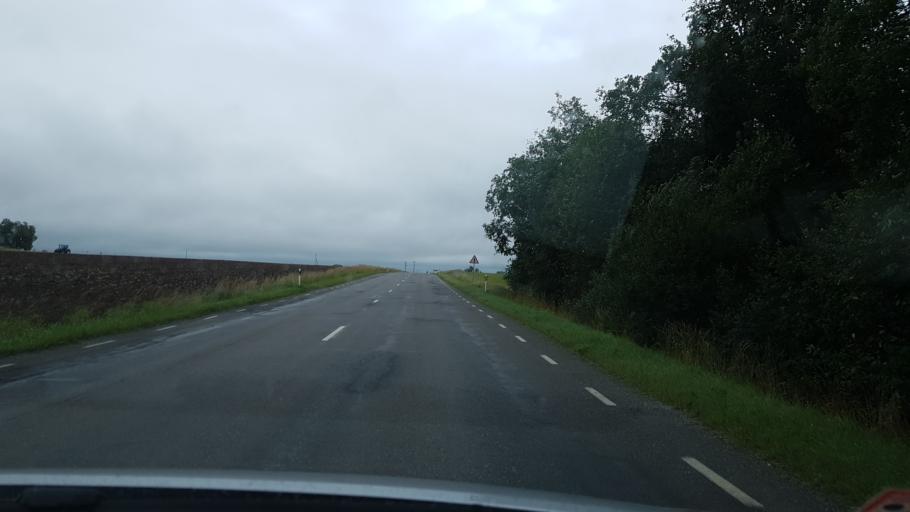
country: EE
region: Vorumaa
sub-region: Antsla vald
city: Vana-Antsla
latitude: 57.9032
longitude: 26.4652
